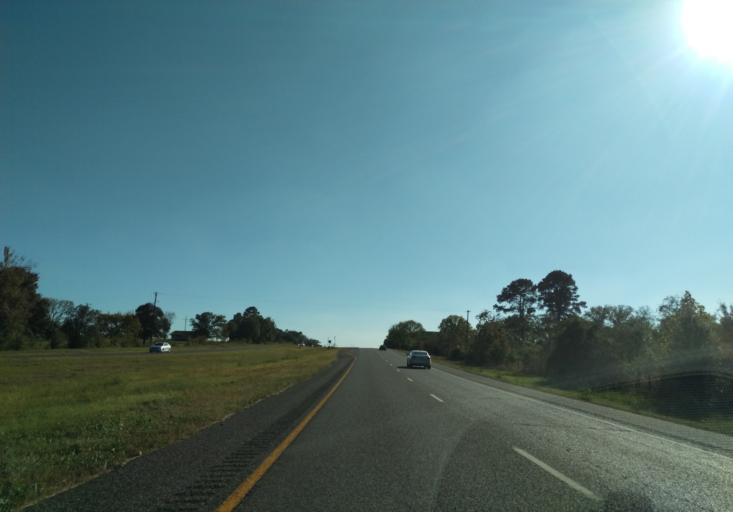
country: US
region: Texas
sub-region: Waller County
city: Hempstead
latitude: 30.2000
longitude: -96.0603
